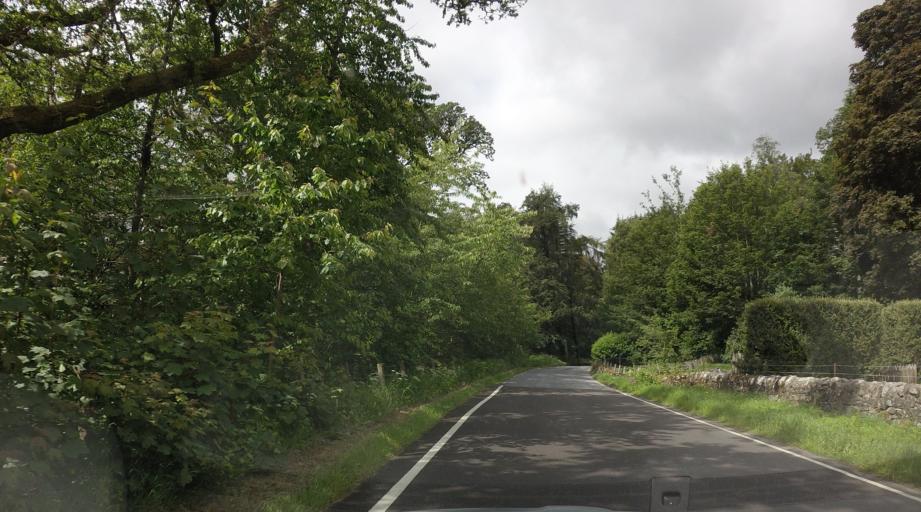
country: GB
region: Scotland
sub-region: Perth and Kinross
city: Pitlochry
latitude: 56.7268
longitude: -3.7796
